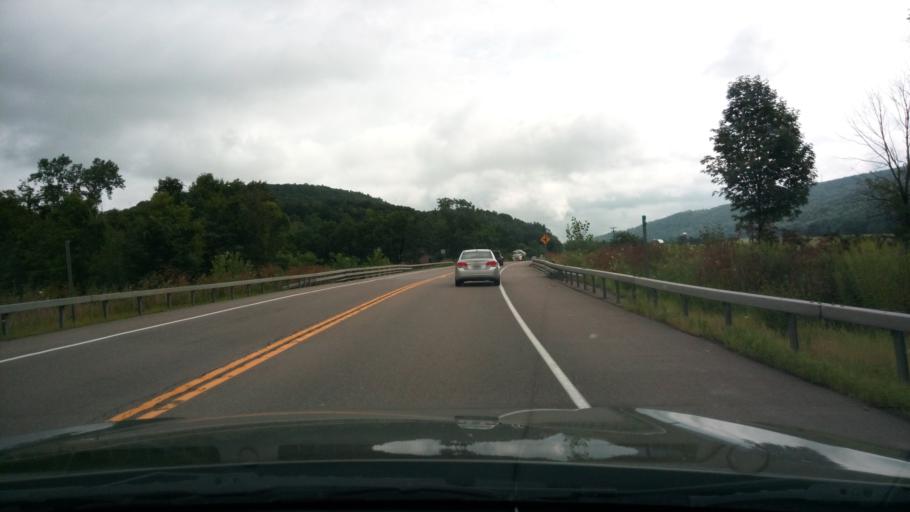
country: US
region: New York
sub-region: Schuyler County
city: Montour Falls
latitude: 42.3230
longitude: -76.6587
